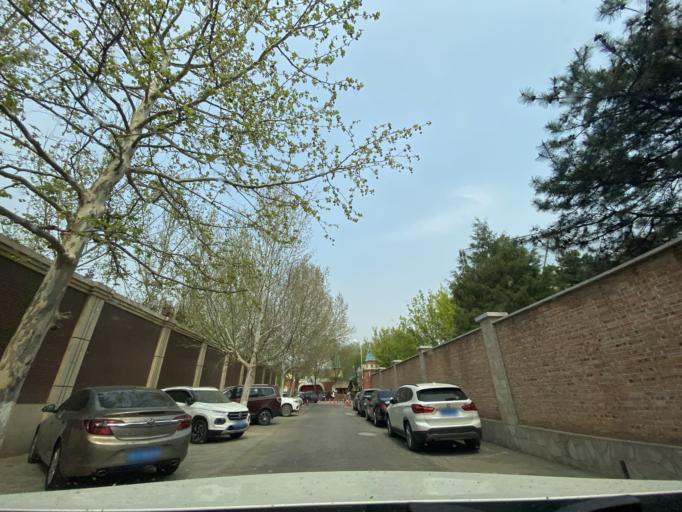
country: CN
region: Beijing
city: Sijiqing
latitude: 39.9423
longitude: 116.2459
